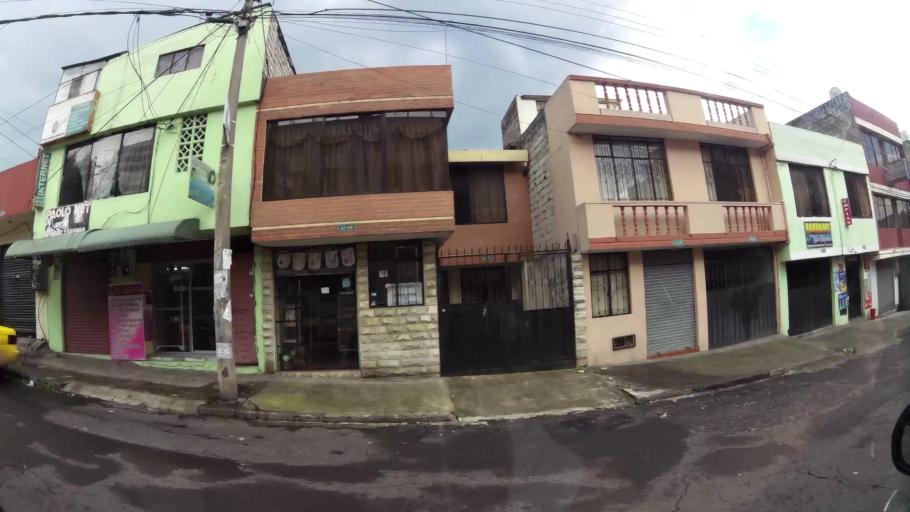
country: EC
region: Pichincha
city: Quito
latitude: -0.2818
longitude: -78.5426
